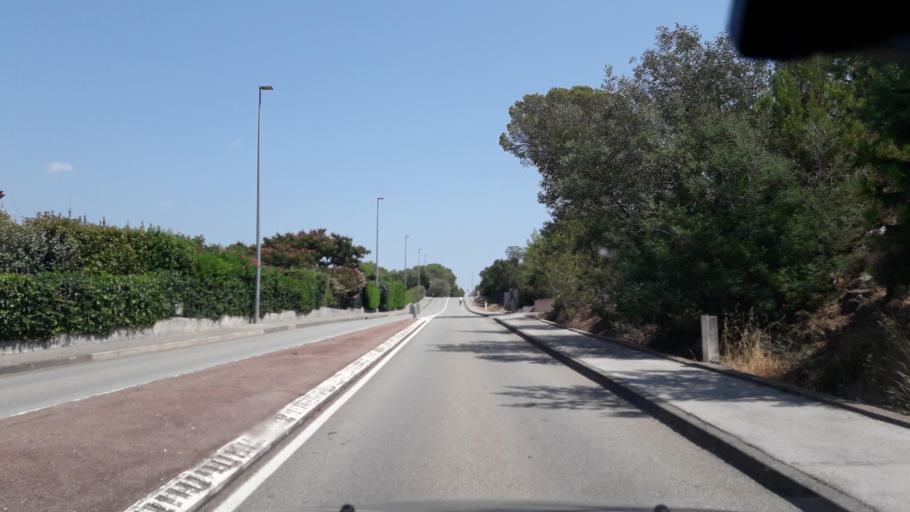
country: FR
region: Provence-Alpes-Cote d'Azur
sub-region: Departement du Var
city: Saint-Raphael
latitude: 43.4403
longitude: 6.7886
